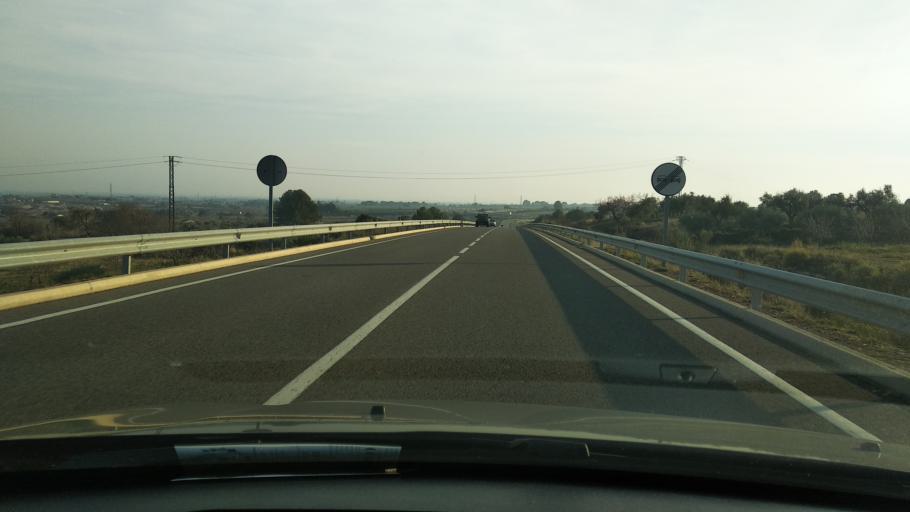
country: ES
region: Catalonia
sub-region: Provincia de Tarragona
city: les Borges del Camp
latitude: 41.1713
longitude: 1.0096
